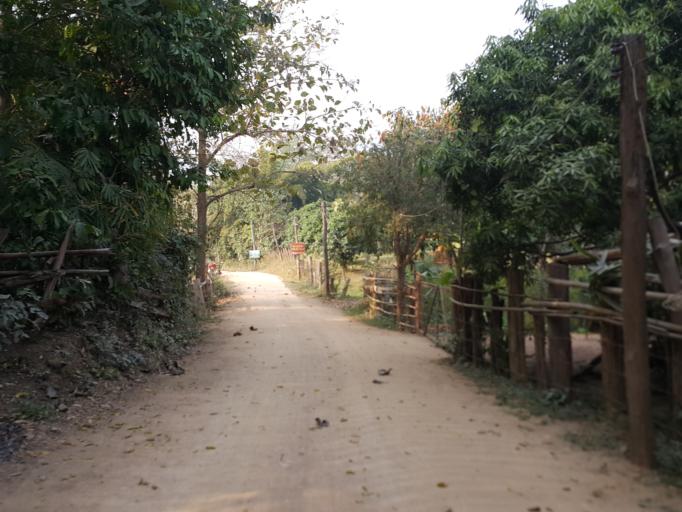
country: TH
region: Lamphun
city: Li
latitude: 17.6069
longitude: 98.9638
